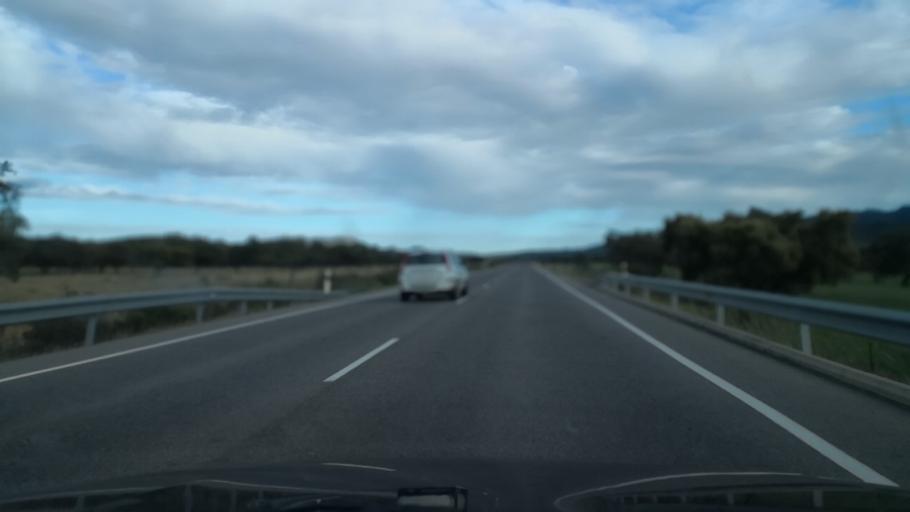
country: ES
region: Extremadura
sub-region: Provincia de Caceres
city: Pedroso de Acim
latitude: 39.8618
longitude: -6.4303
